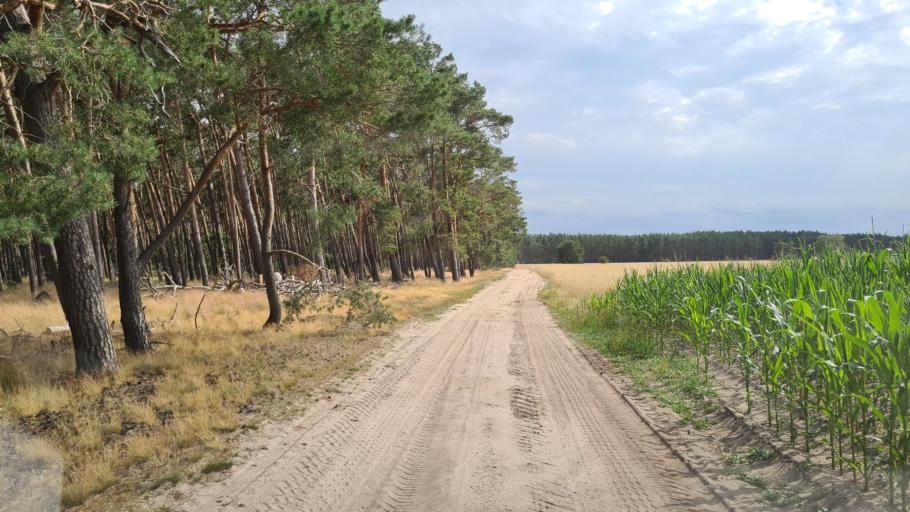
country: DE
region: Saxony-Anhalt
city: Holzdorf
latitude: 51.8170
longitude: 13.1950
